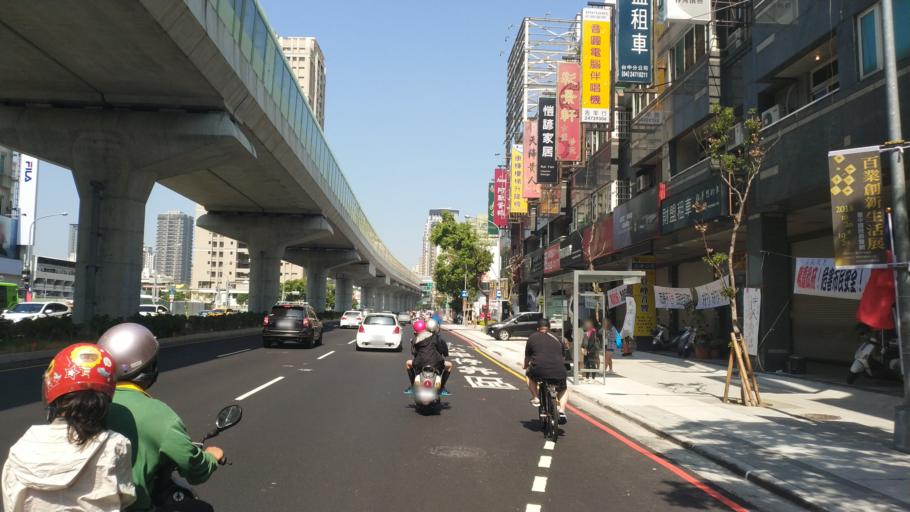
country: TW
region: Taiwan
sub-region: Taichung City
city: Taichung
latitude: 24.1363
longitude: 120.6467
